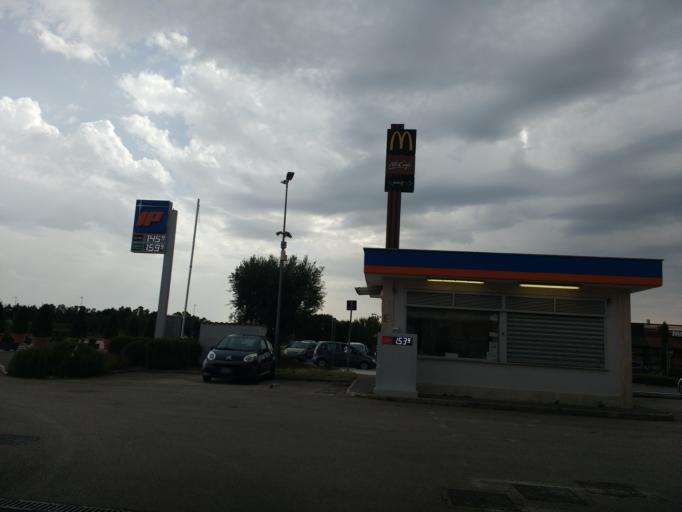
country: IT
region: Latium
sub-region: Citta metropolitana di Roma Capitale
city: Monte Migliore-La Selvotta
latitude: 41.7155
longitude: 12.4441
